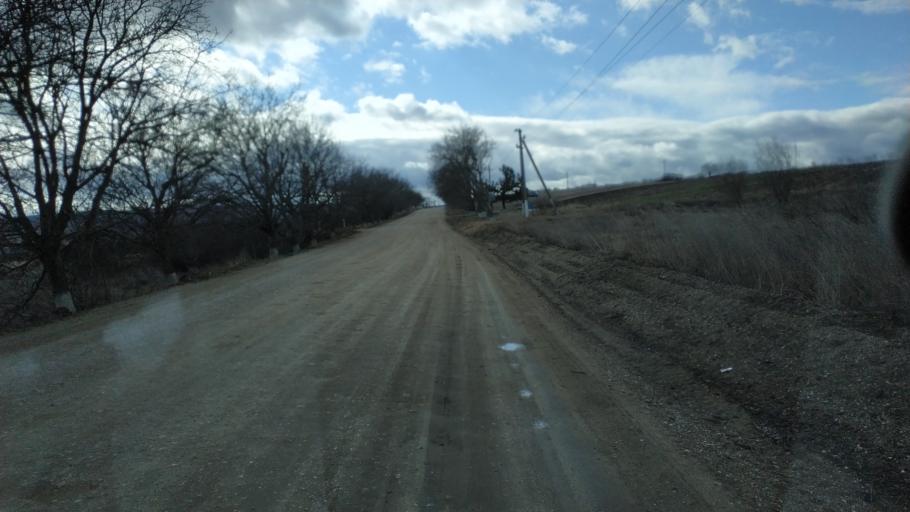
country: MD
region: Stinga Nistrului
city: Bucovat
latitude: 47.1966
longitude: 28.4892
